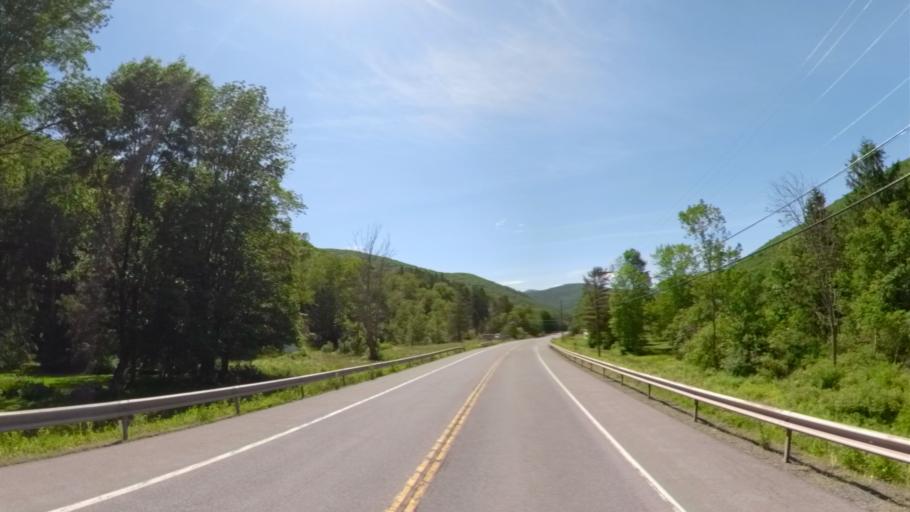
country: US
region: New York
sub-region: Ulster County
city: Shokan
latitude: 42.1208
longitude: -74.4602
